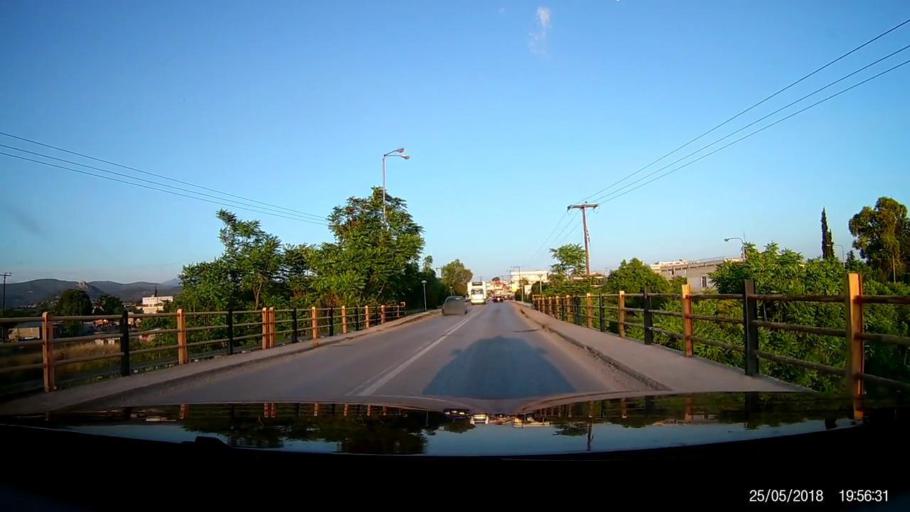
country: GR
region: Central Greece
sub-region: Nomos Evvoias
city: Vasilikon
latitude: 38.4283
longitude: 23.6620
